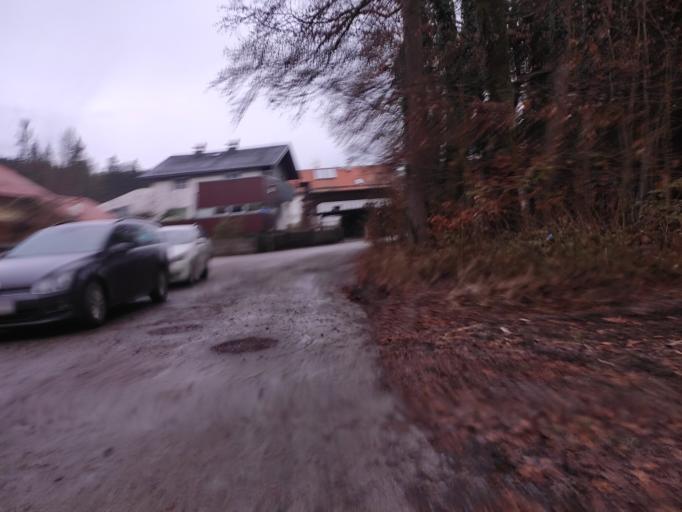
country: AT
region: Salzburg
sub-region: Politischer Bezirk Salzburg-Umgebung
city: Elixhausen
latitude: 47.8615
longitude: 13.0543
